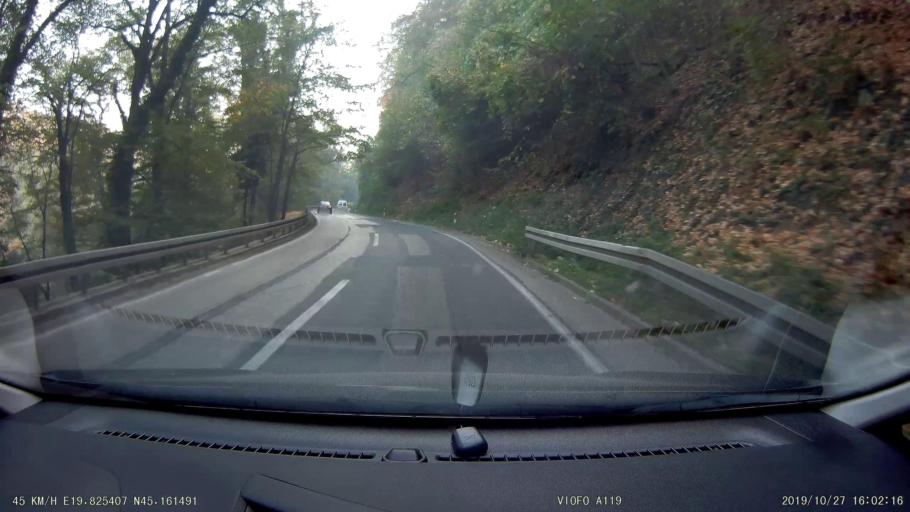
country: RS
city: Vrdnik
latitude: 45.1614
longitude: 19.8254
